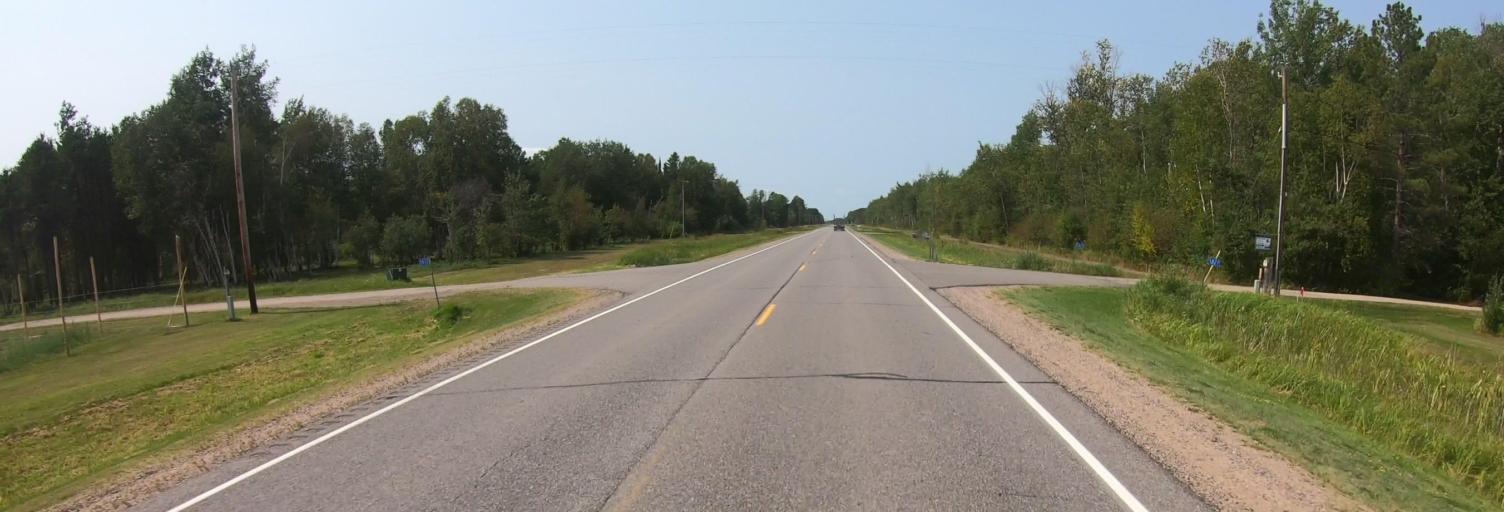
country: US
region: Minnesota
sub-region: Koochiching County
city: International Falls
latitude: 48.5190
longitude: -93.6051
